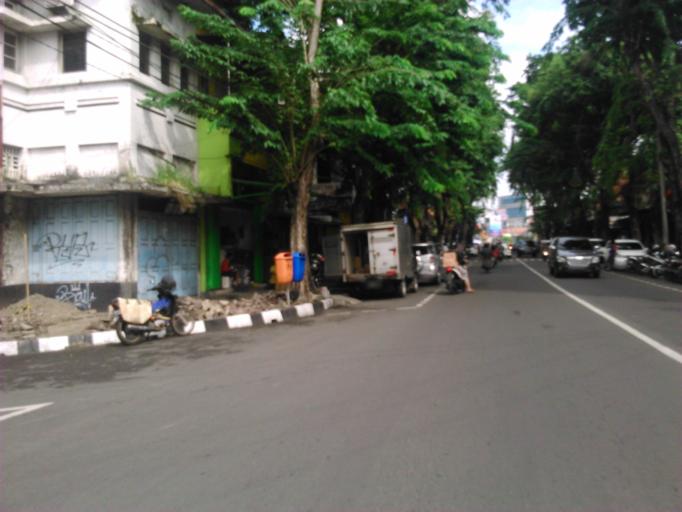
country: ID
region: East Java
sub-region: Kota Surabaya
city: Surabaya
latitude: -7.2603
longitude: 112.7449
